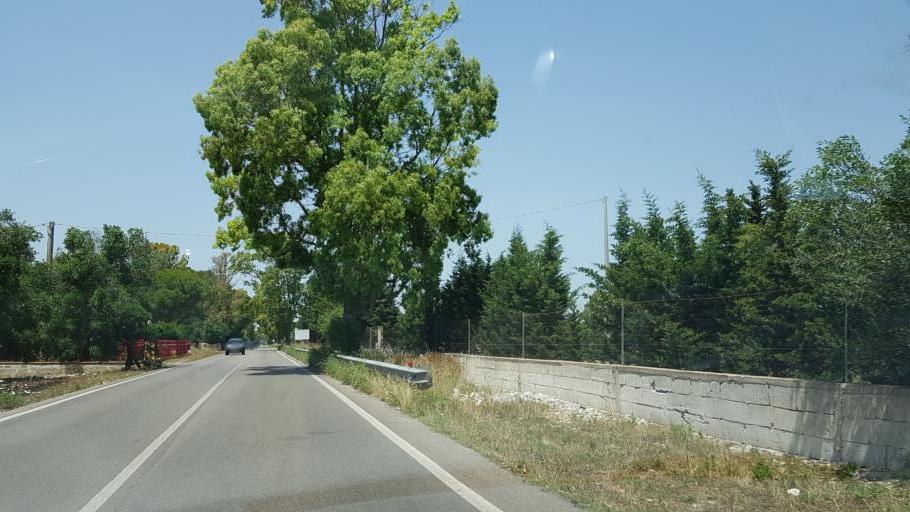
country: IT
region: Apulia
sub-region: Provincia di Lecce
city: Porto Cesareo
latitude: 40.2598
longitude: 17.9225
